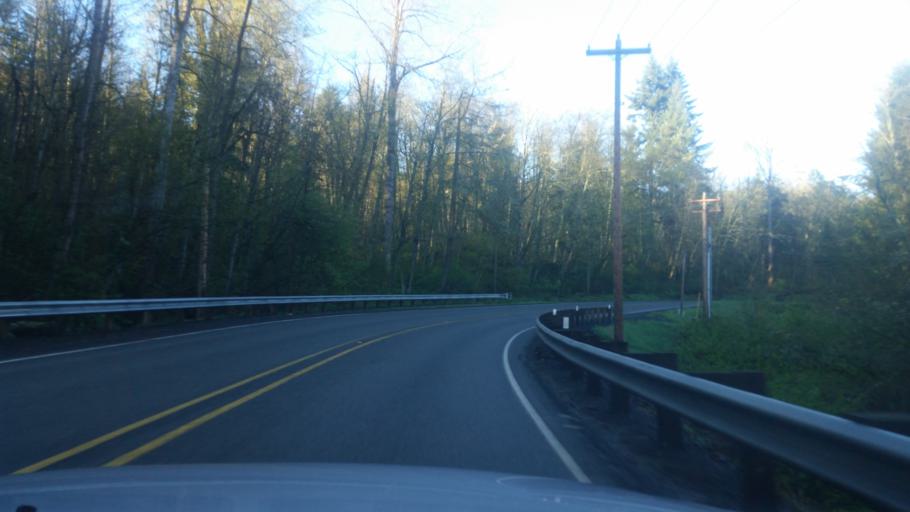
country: US
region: Washington
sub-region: Pierce County
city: Eatonville
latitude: 46.8540
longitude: -122.2645
